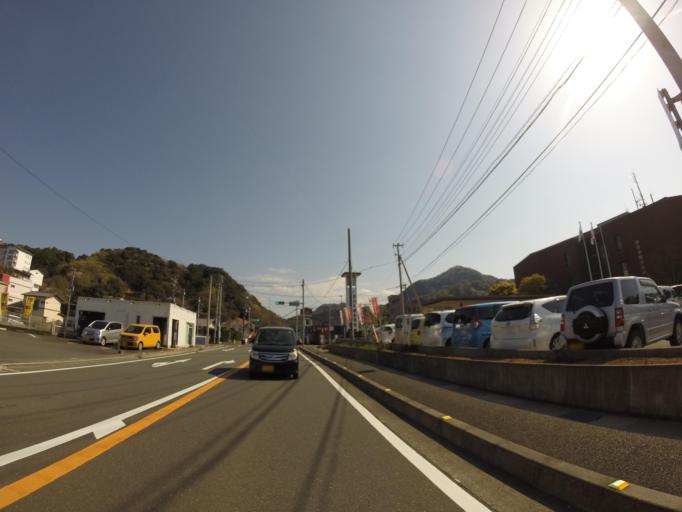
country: JP
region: Shizuoka
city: Mishima
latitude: 35.0281
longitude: 138.9296
